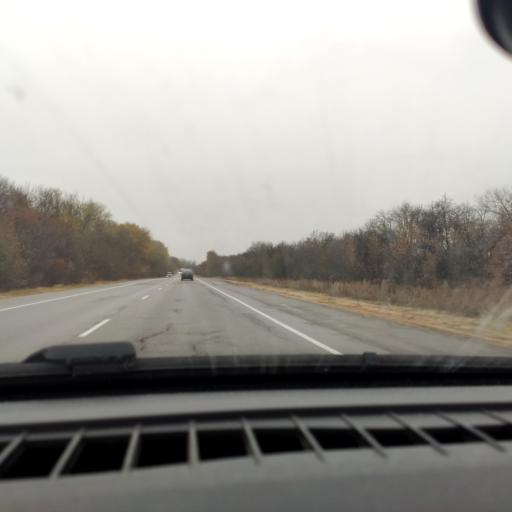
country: RU
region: Voronezj
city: Kolodeznyy
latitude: 51.2793
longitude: 39.0444
